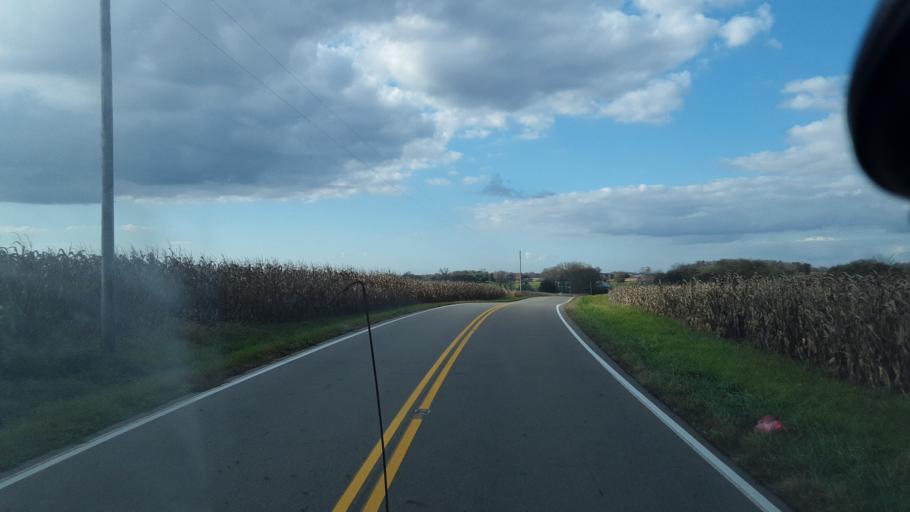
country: US
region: Ohio
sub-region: Highland County
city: Greenfield
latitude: 39.4221
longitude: -83.4440
